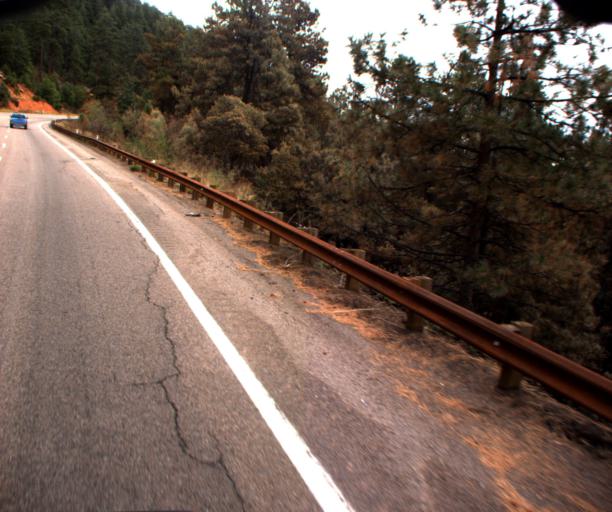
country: US
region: Arizona
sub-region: Gila County
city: Star Valley
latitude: 34.3048
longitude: -110.9243
